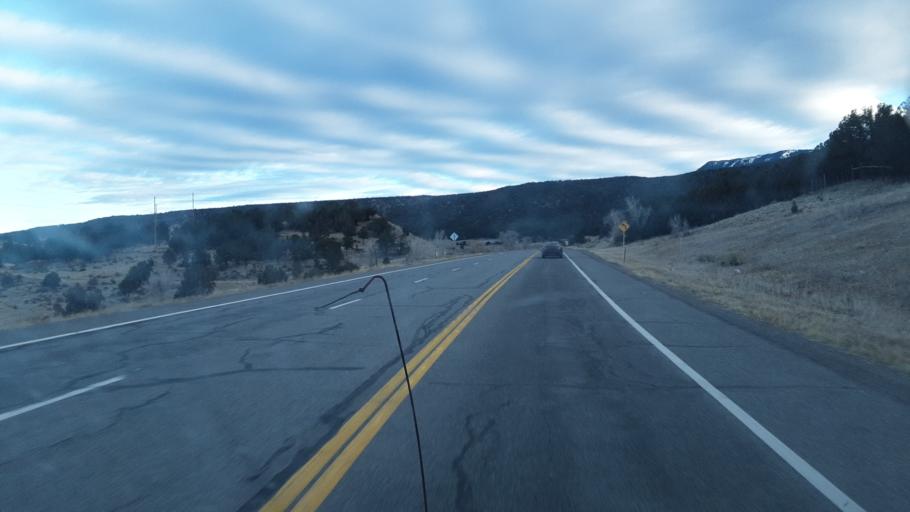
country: US
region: Colorado
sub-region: Ouray County
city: Ouray
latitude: 38.2224
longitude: -107.7281
